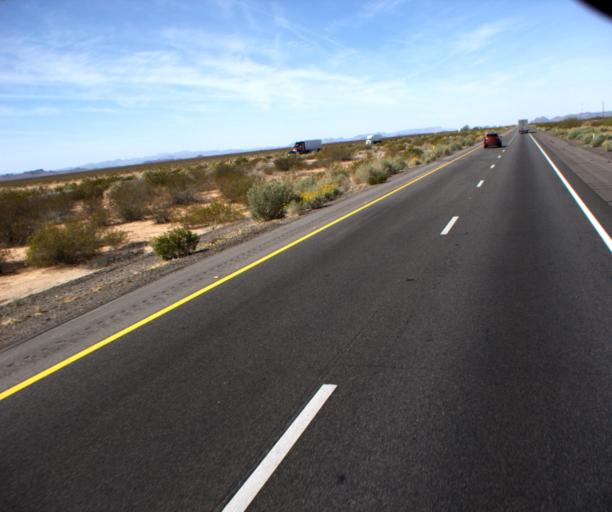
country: US
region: Arizona
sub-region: La Paz County
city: Salome
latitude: 33.5823
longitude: -113.4394
